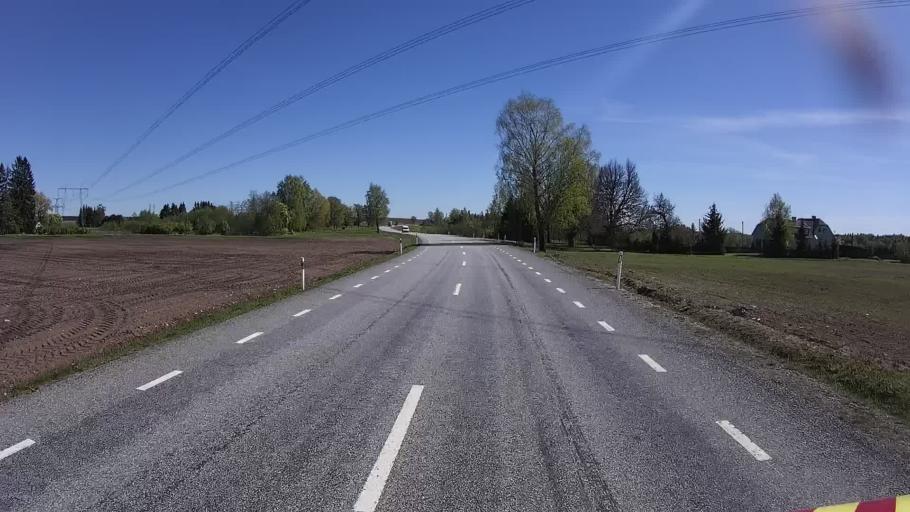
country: EE
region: Laeaene-Virumaa
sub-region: Tapa vald
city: Tapa
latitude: 59.2343
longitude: 25.7060
